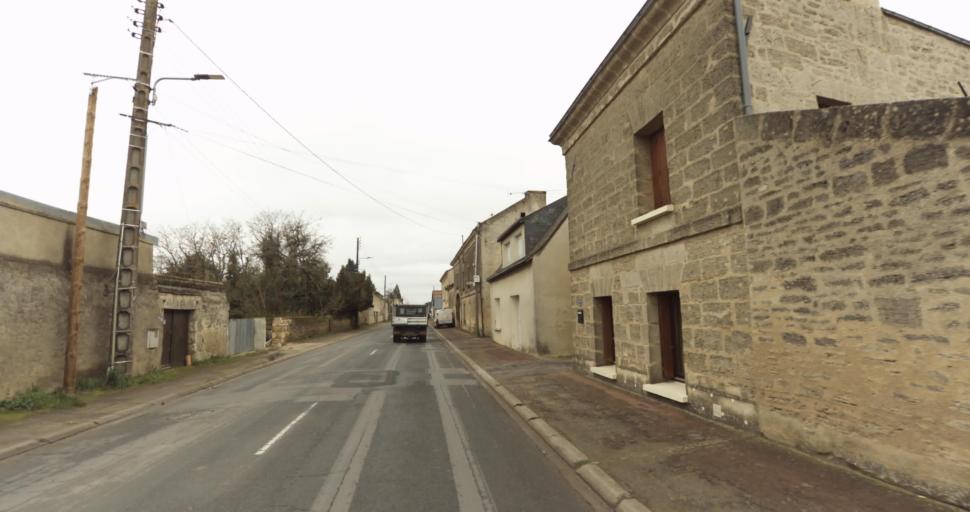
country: FR
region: Pays de la Loire
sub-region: Departement de Maine-et-Loire
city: Doue-la-Fontaine
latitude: 47.1884
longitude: -0.2615
